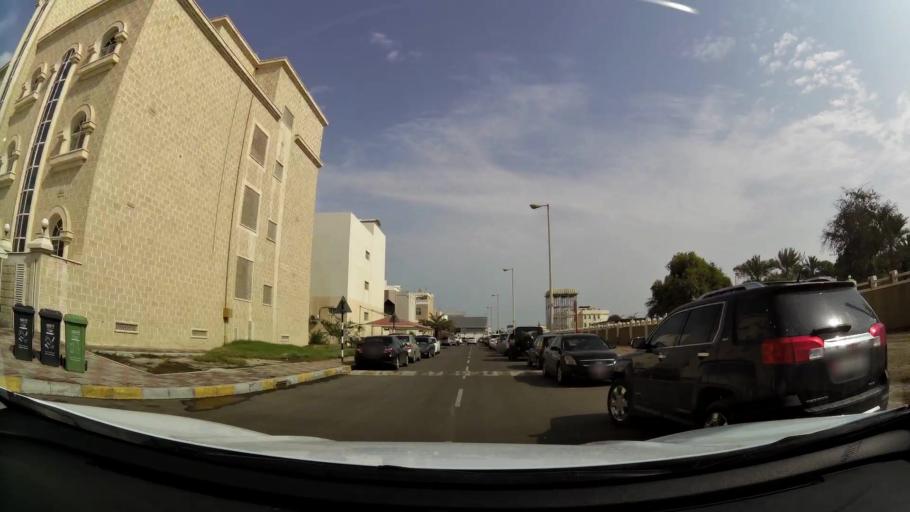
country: AE
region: Abu Dhabi
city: Abu Dhabi
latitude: 24.4380
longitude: 54.4192
